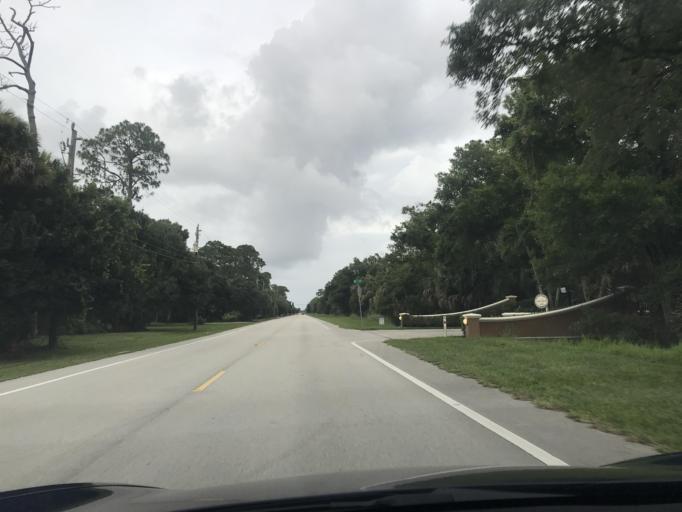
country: US
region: Florida
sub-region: Indian River County
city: West Vero Corridor
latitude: 27.6168
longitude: -80.4605
